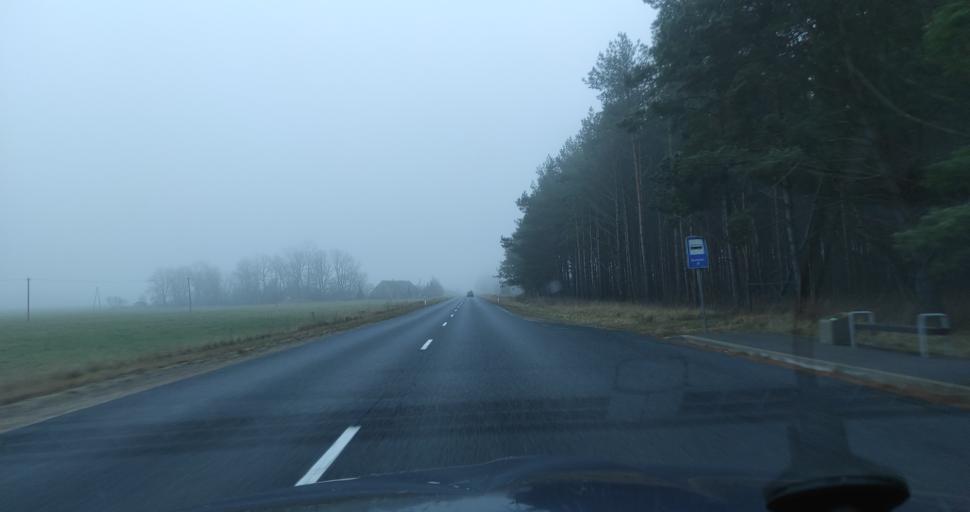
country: LV
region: Alsunga
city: Alsunga
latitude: 57.1042
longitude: 21.4228
